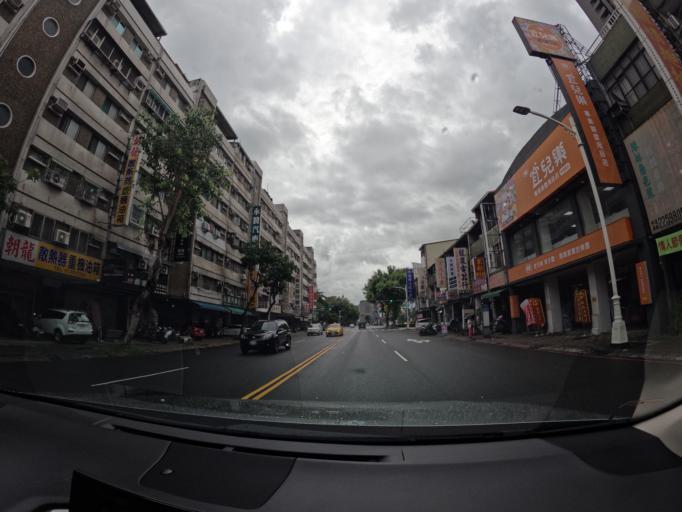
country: TW
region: Kaohsiung
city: Kaohsiung
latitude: 22.6340
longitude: 120.3190
